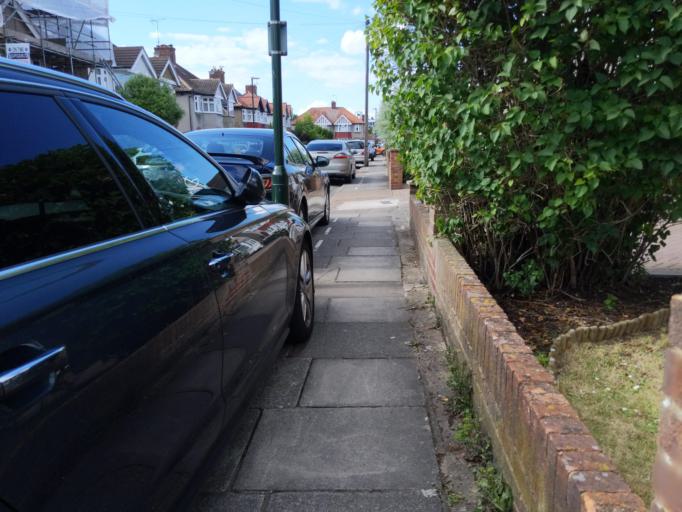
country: GB
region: England
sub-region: Greater London
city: Hounslow
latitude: 51.4505
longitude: -0.3598
